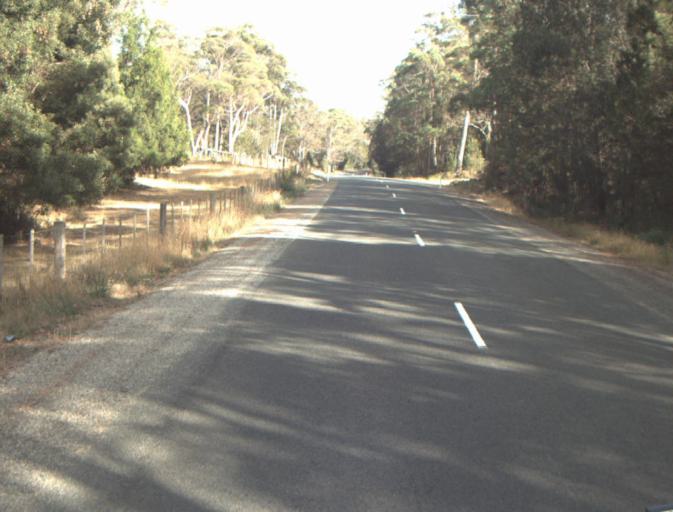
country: AU
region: Tasmania
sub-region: Dorset
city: Bridport
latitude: -41.1258
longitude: 147.2101
